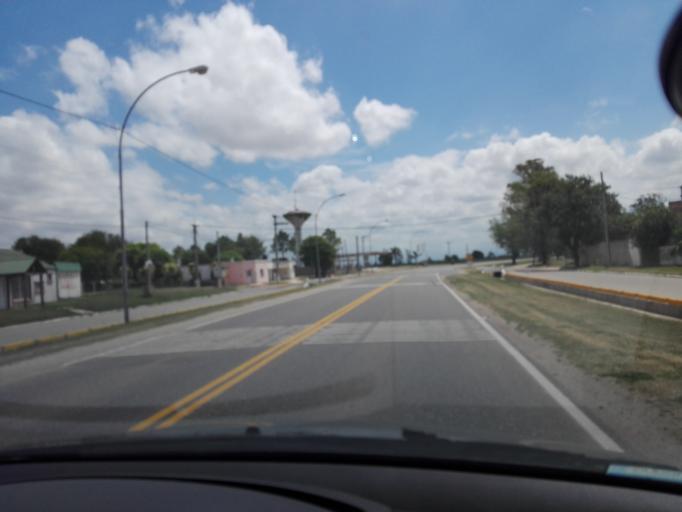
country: AR
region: Cordoba
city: Toledo
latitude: -31.6502
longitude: -64.0897
